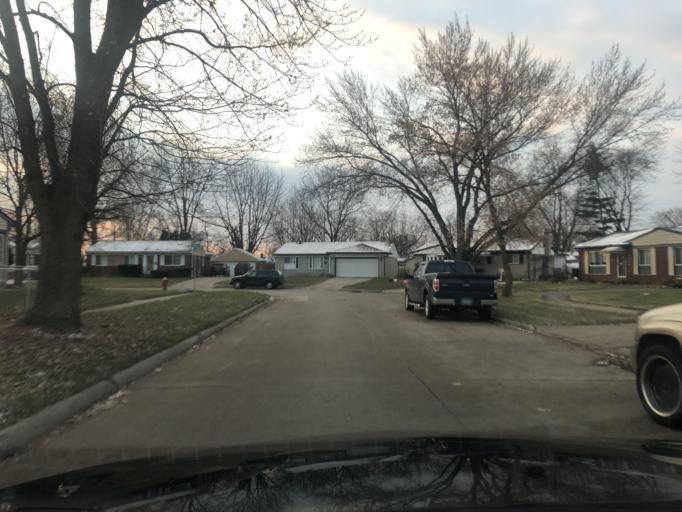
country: US
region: Michigan
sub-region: Wayne County
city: Romulus
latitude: 42.2330
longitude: -83.3821
